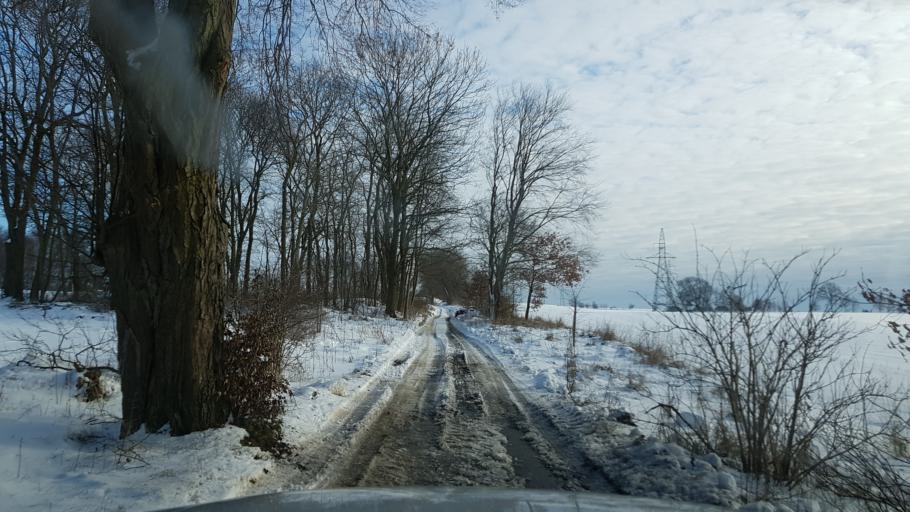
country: PL
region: West Pomeranian Voivodeship
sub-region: Powiat drawski
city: Drawsko Pomorskie
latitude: 53.5344
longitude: 15.7752
